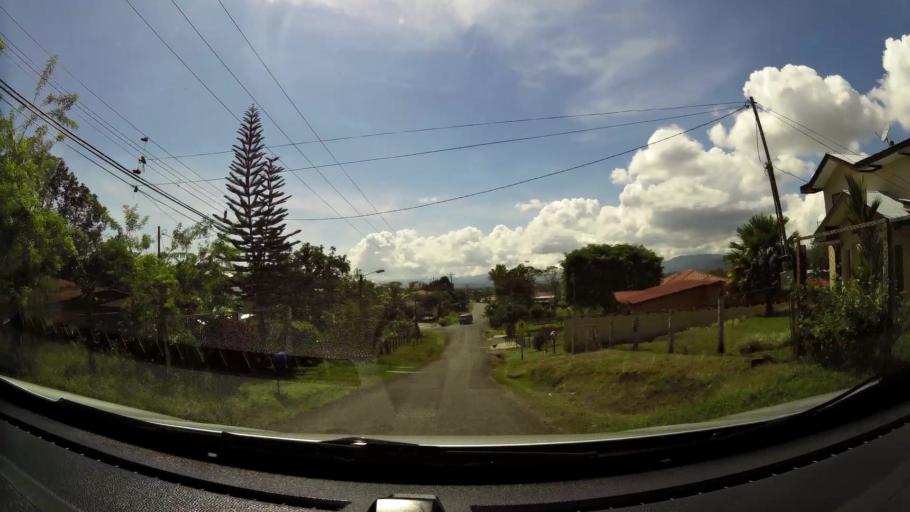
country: CR
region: San Jose
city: San Isidro
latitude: 9.3860
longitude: -83.6978
